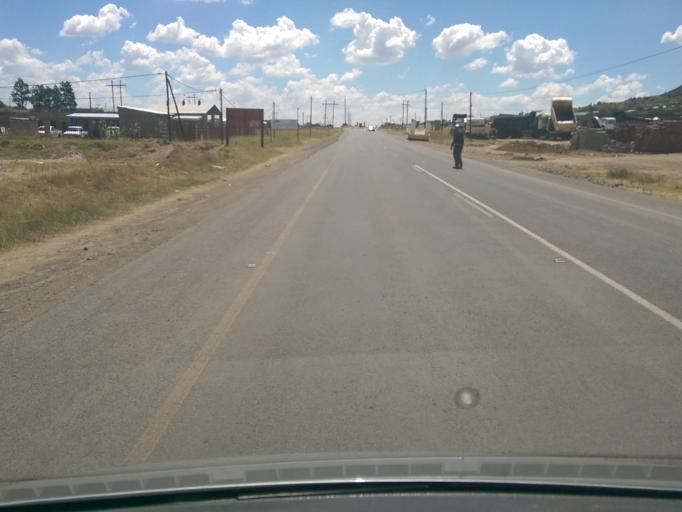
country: LS
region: Maseru
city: Maseru
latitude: -29.3665
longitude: 27.4717
